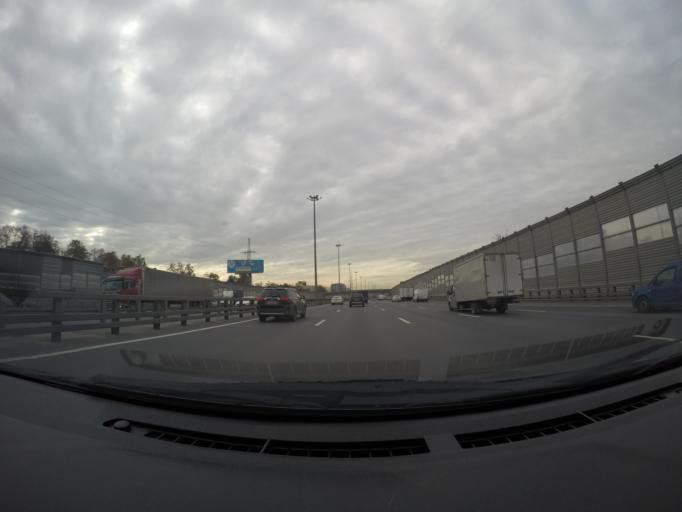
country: RU
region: Moskovskaya
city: Druzhba
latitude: 55.8908
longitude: 37.7422
